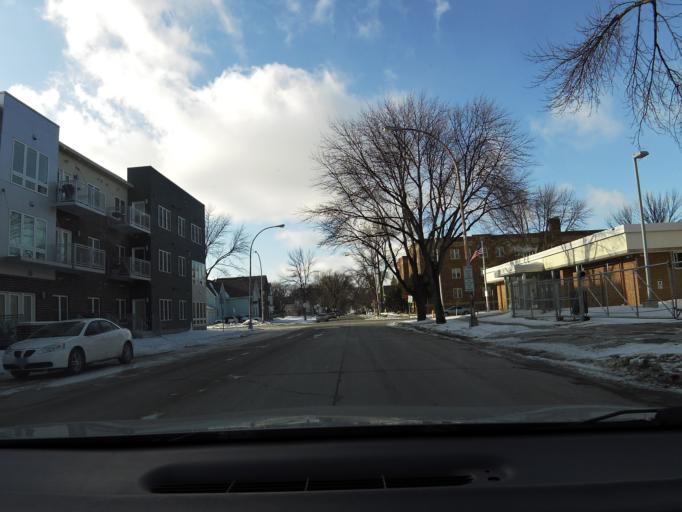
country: US
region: North Dakota
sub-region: Grand Forks County
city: Grand Forks
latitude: 47.9238
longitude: -97.0352
